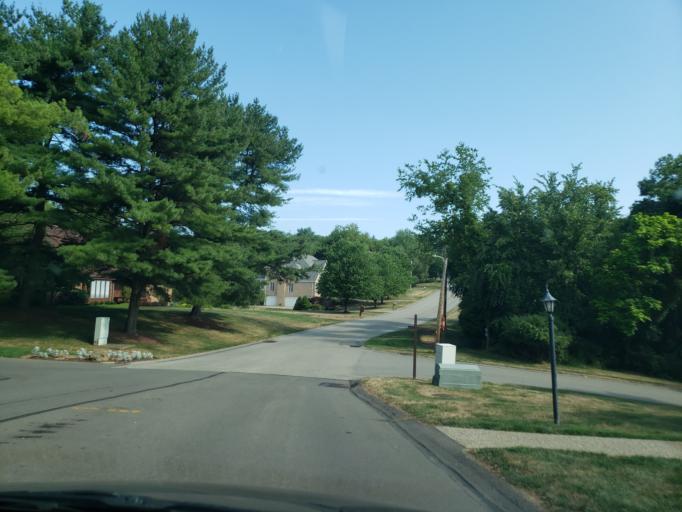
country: US
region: Pennsylvania
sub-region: Allegheny County
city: Coraopolis
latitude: 40.5410
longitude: -80.1510
